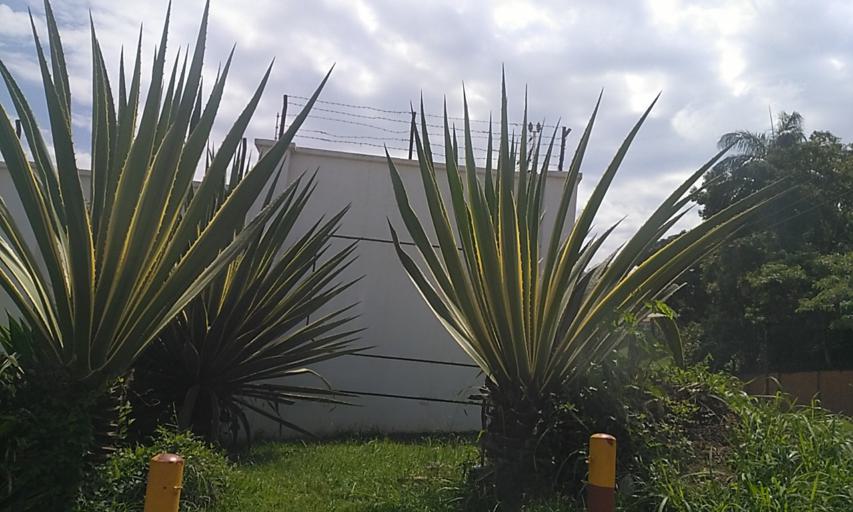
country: UG
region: Central Region
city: Kampala Central Division
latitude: 0.3371
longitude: 32.5933
